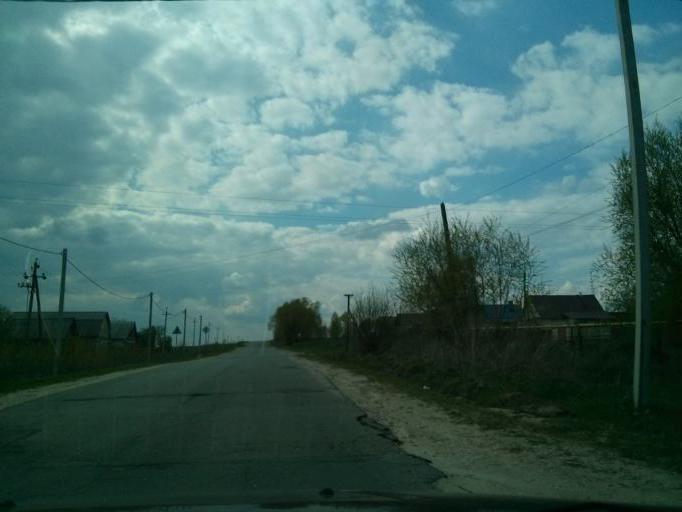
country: RU
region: Nizjnij Novgorod
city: Shimorskoye
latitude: 55.3347
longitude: 41.9228
